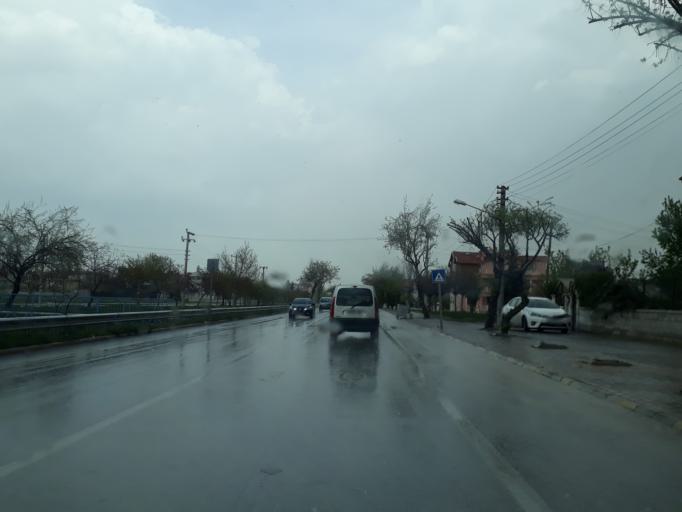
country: TR
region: Konya
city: Selcuklu
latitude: 37.9208
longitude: 32.4873
